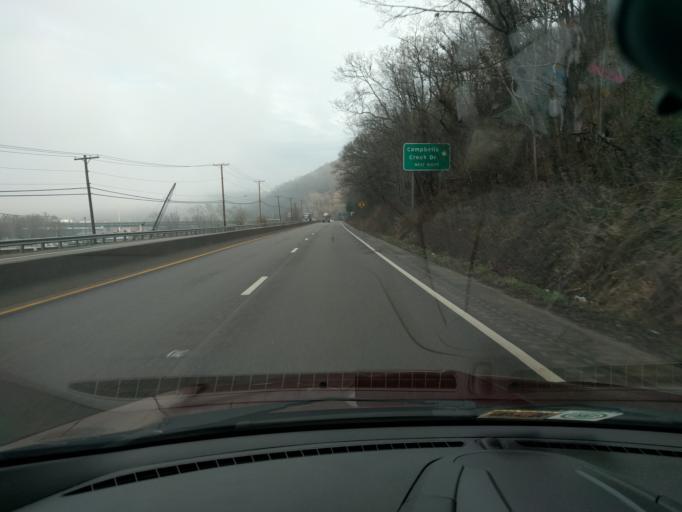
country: US
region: West Virginia
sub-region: Kanawha County
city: Rand
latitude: 38.3050
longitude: -81.5560
